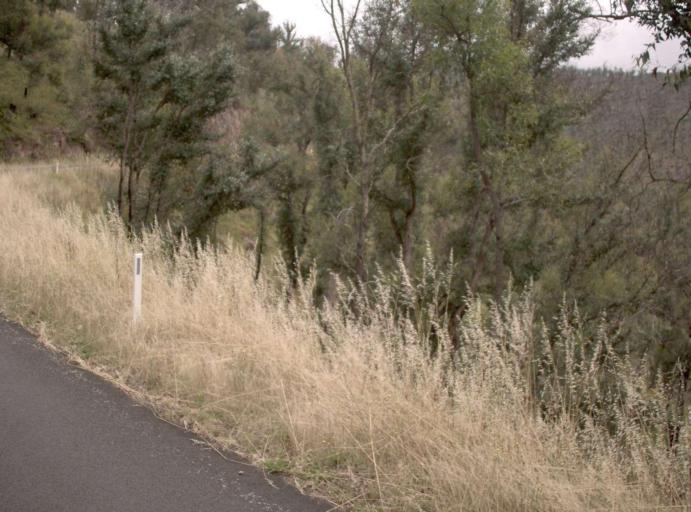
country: AU
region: Victoria
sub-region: Wellington
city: Heyfield
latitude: -37.7194
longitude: 146.6675
